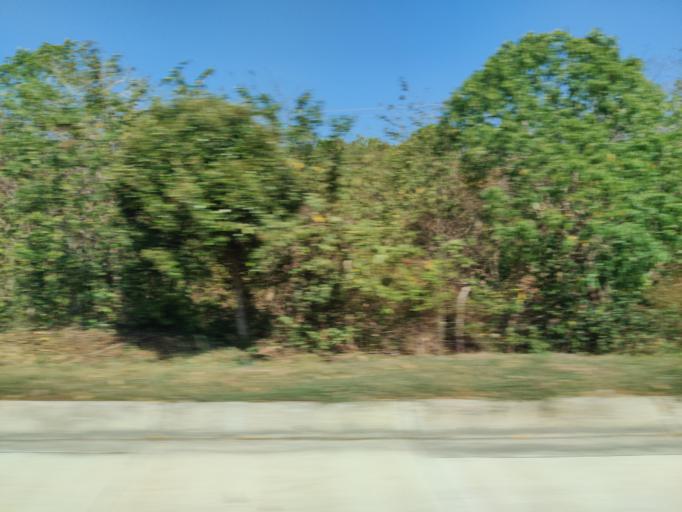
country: CO
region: Atlantico
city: Juan de Acosta
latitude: 10.8467
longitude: -75.1310
